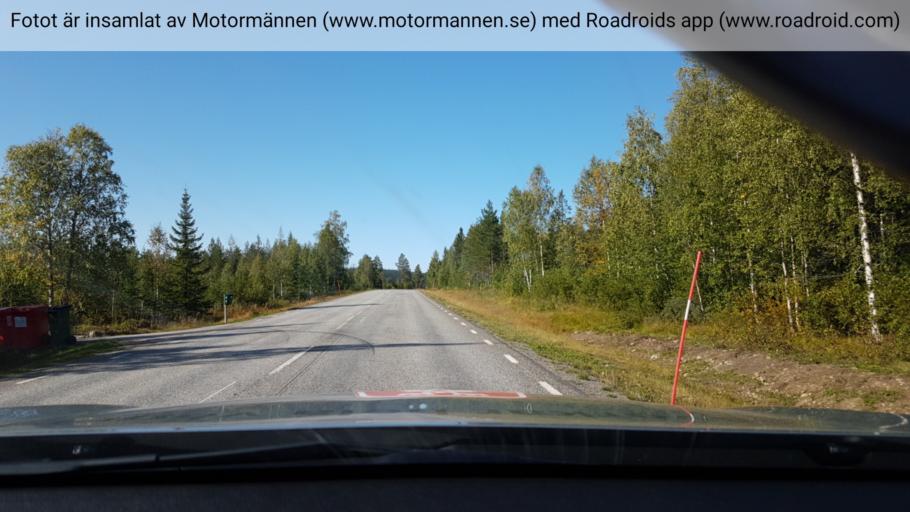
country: SE
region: Vaesterbotten
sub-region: Norsjo Kommun
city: Norsjoe
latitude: 64.9323
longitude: 19.4075
